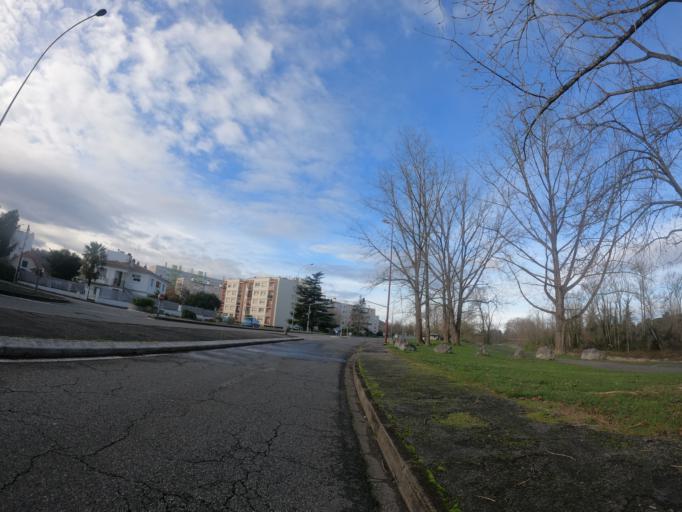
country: FR
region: Aquitaine
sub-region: Departement des Pyrenees-Atlantiques
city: Jurancon
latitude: 43.2918
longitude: -0.3934
